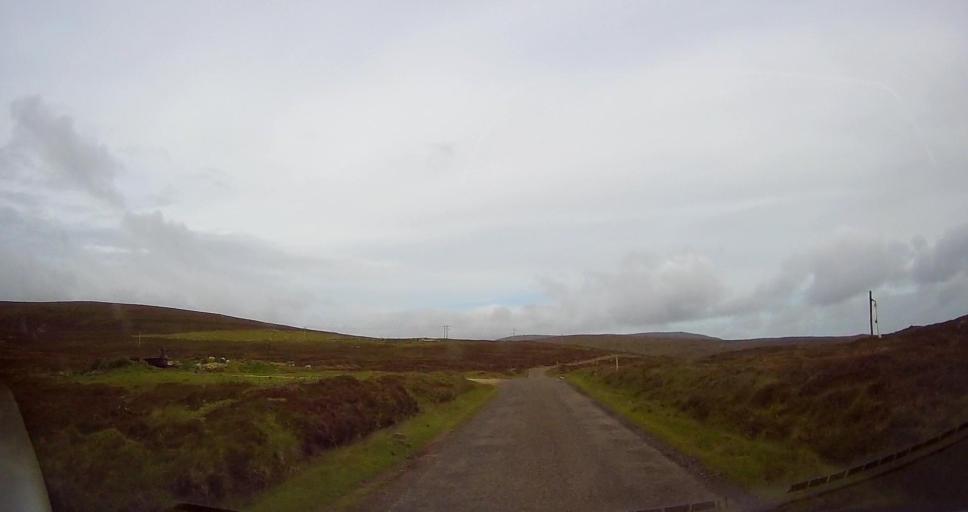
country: GB
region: Scotland
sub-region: Orkney Islands
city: Stromness
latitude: 58.8539
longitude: -3.2082
